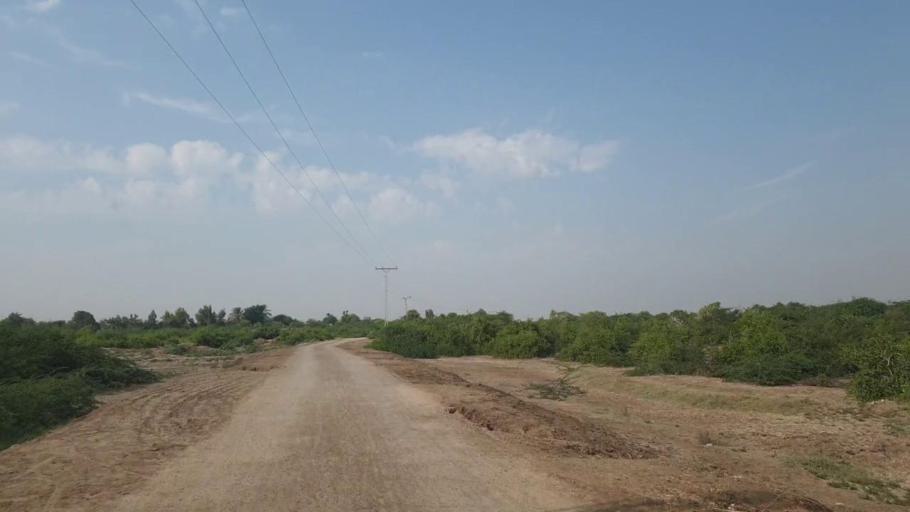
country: PK
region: Sindh
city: Digri
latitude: 25.0073
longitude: 69.0644
